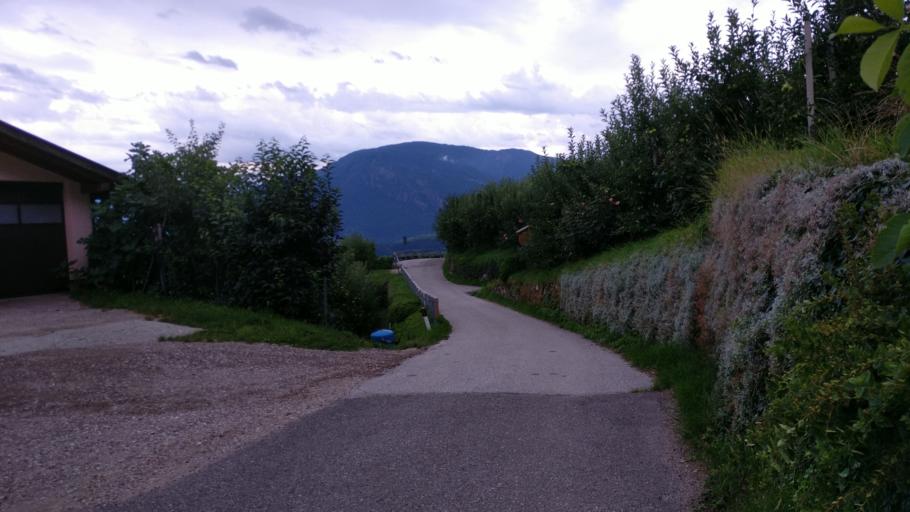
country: IT
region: Trentino-Alto Adige
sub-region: Bolzano
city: San Paolo
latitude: 46.4879
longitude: 11.2476
